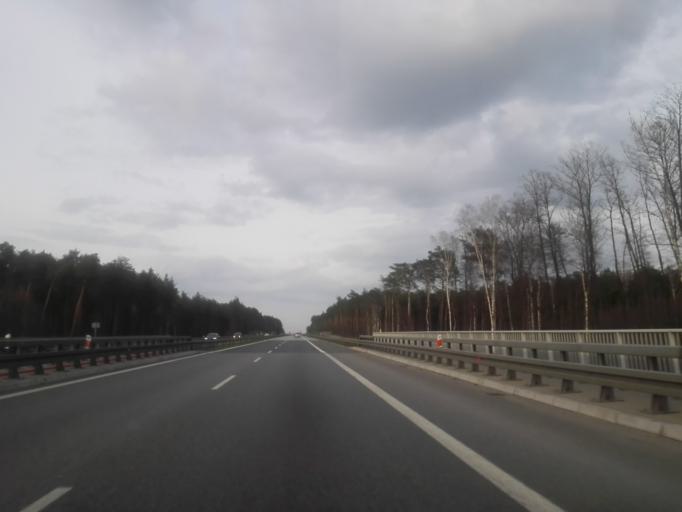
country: PL
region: Lodz Voivodeship
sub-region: Powiat tomaszowski
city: Czerniewice
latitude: 51.6323
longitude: 20.1090
